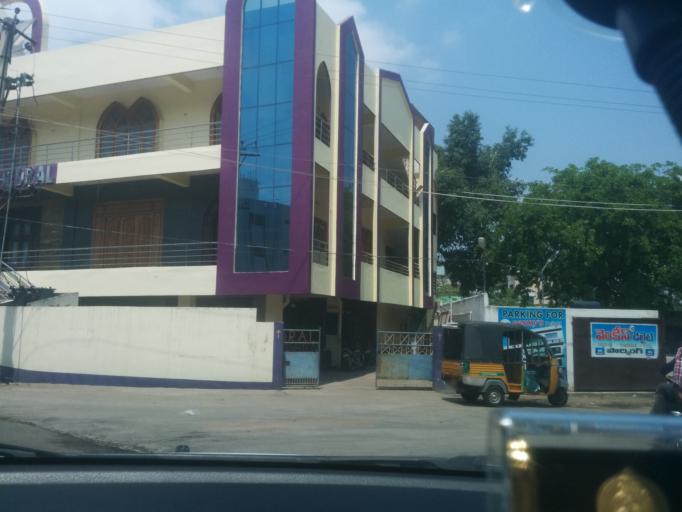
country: IN
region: Andhra Pradesh
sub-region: East Godavari
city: Rajahmundry
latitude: 17.0116
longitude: 81.7813
